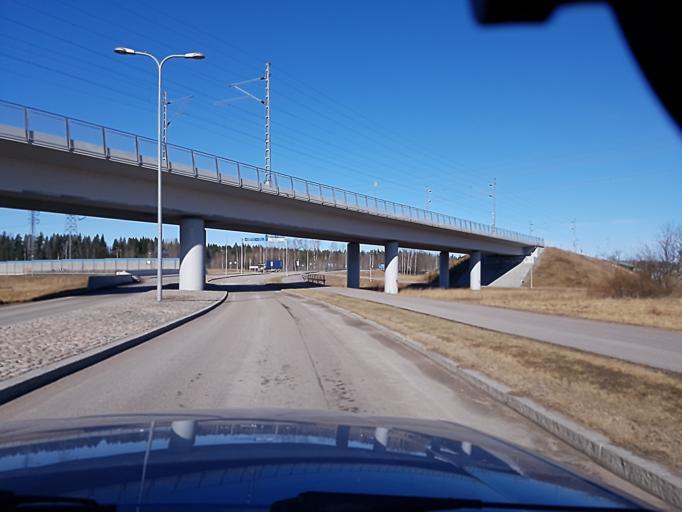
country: FI
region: Uusimaa
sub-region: Helsinki
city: Kilo
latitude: 60.2890
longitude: 24.8468
